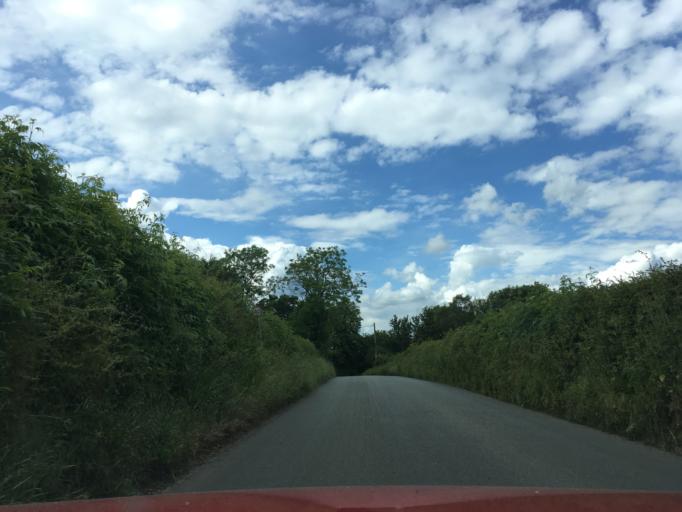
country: GB
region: England
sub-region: Wiltshire
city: Minety
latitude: 51.6500
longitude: -1.9379
